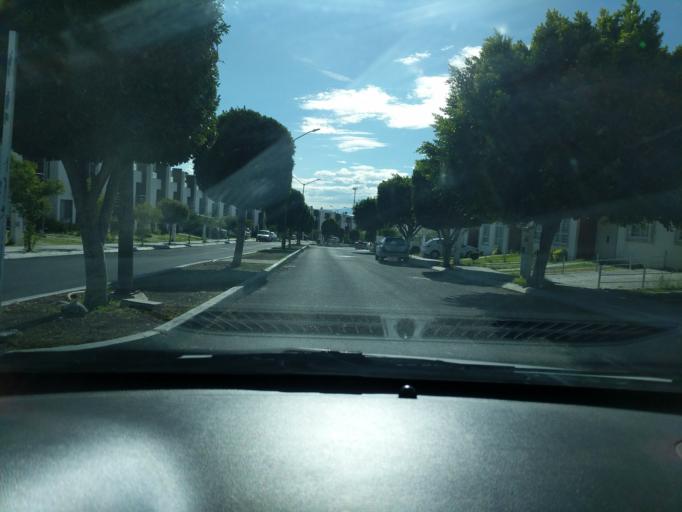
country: MX
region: Queretaro
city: La Canada
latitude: 20.5851
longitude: -100.3366
